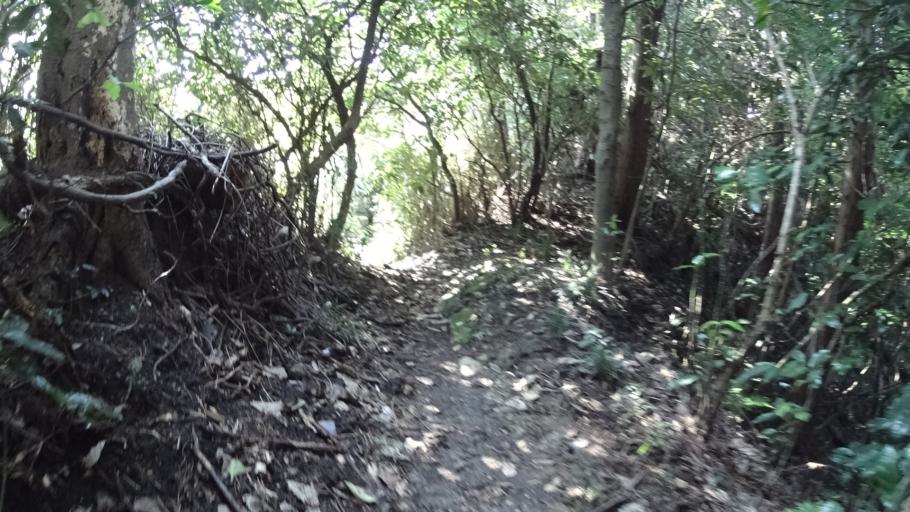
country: JP
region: Kanagawa
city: Zushi
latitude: 35.2926
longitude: 139.6224
